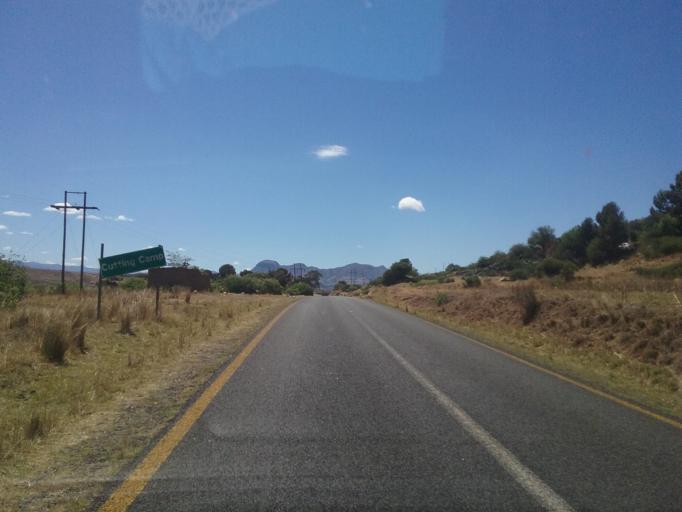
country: LS
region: Quthing
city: Quthing
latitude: -30.2776
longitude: 27.7416
